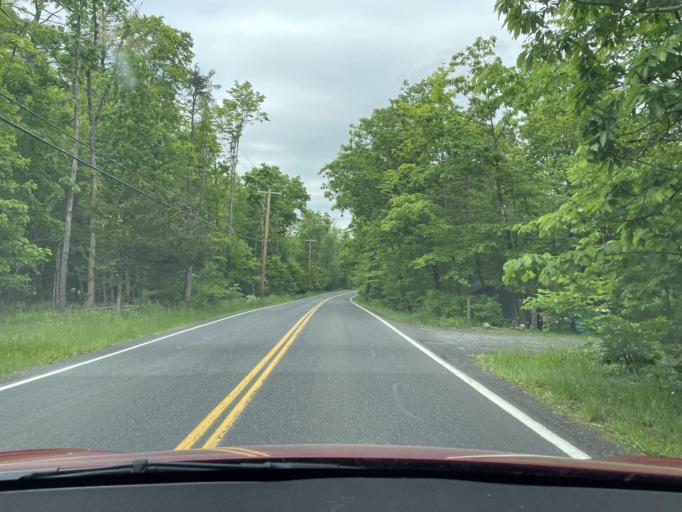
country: US
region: New York
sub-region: Ulster County
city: West Hurley
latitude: 42.0102
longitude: -74.1164
